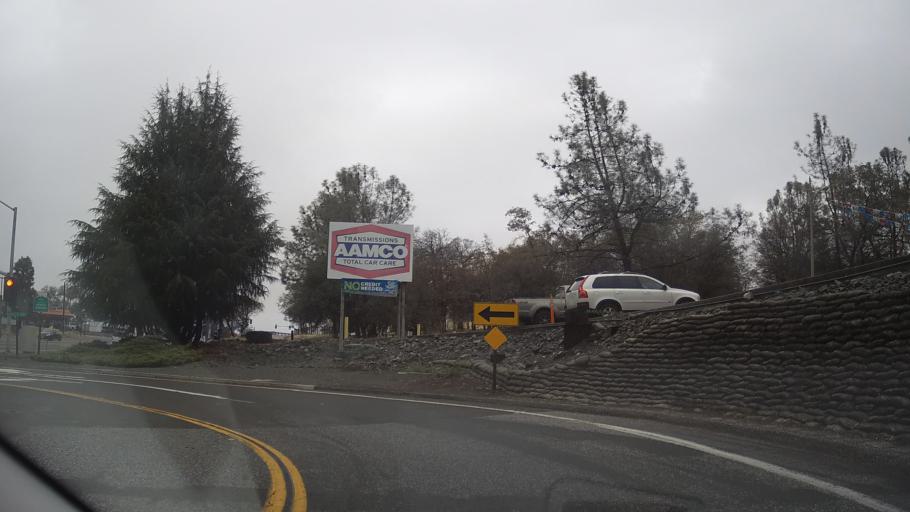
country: US
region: California
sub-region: Placer County
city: North Auburn
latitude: 38.9186
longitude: -121.0808
